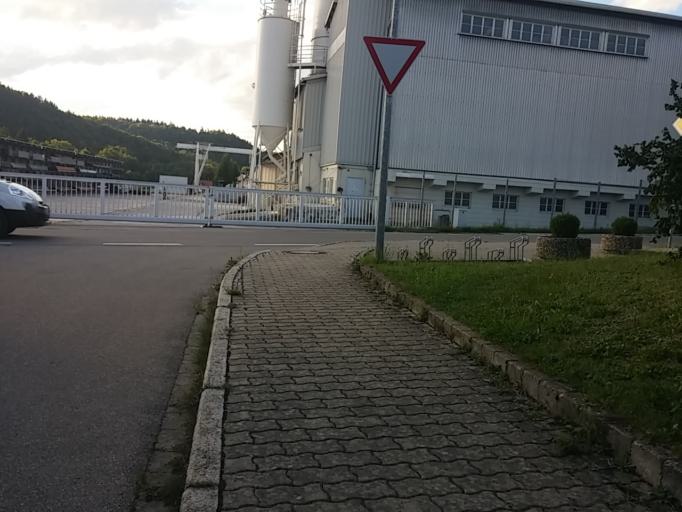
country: DE
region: Baden-Wuerttemberg
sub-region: Tuebingen Region
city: Aitrach
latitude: 47.9353
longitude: 10.0845
